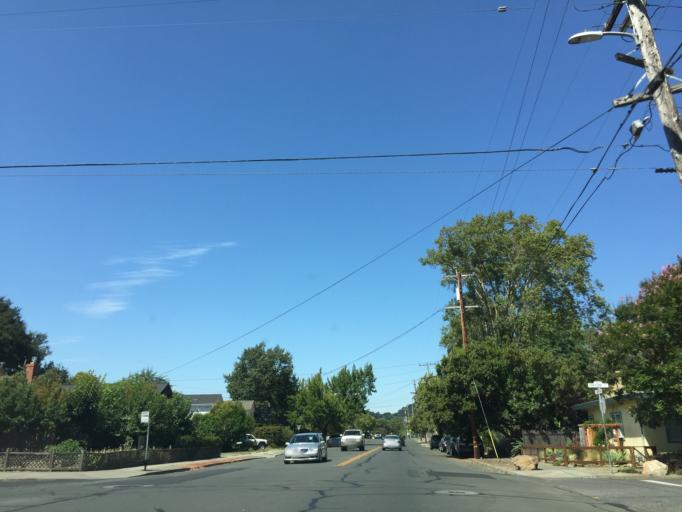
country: US
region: California
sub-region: Napa County
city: Napa
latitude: 38.2878
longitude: -122.2953
